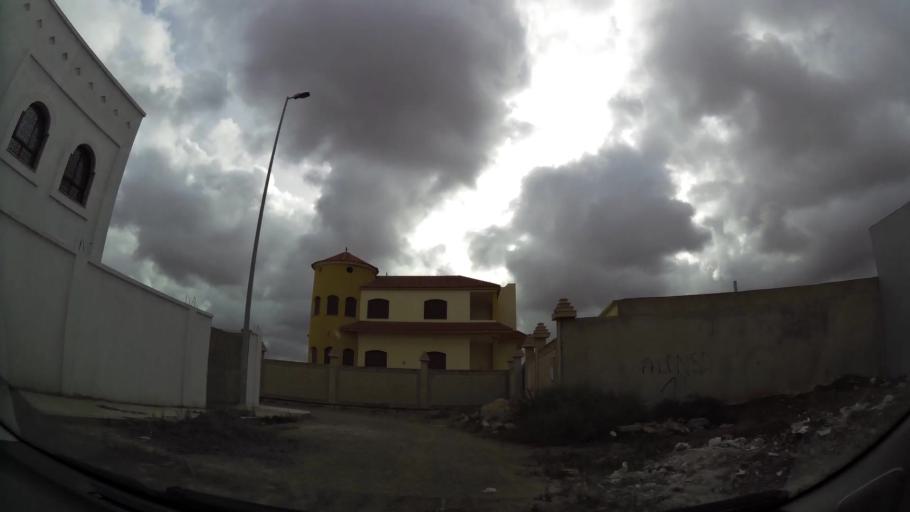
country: MA
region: Oriental
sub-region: Nador
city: Nador
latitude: 35.1625
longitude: -2.9179
